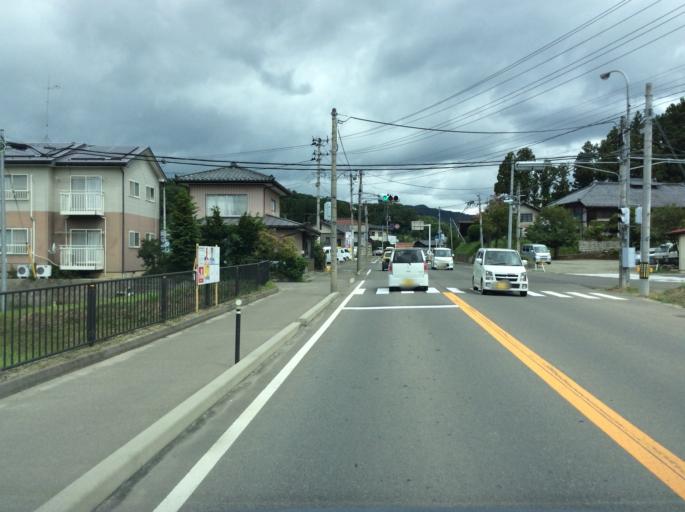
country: JP
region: Fukushima
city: Fukushima-shi
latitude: 37.6747
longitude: 140.5656
